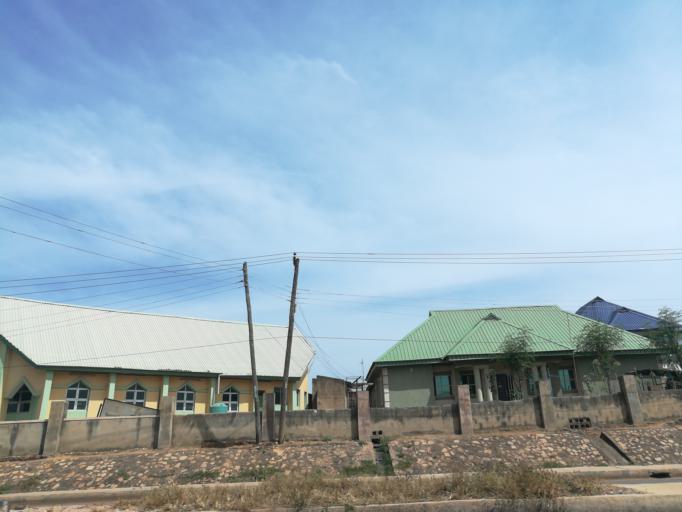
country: NG
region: Plateau
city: Bukuru
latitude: 9.7972
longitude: 8.8594
